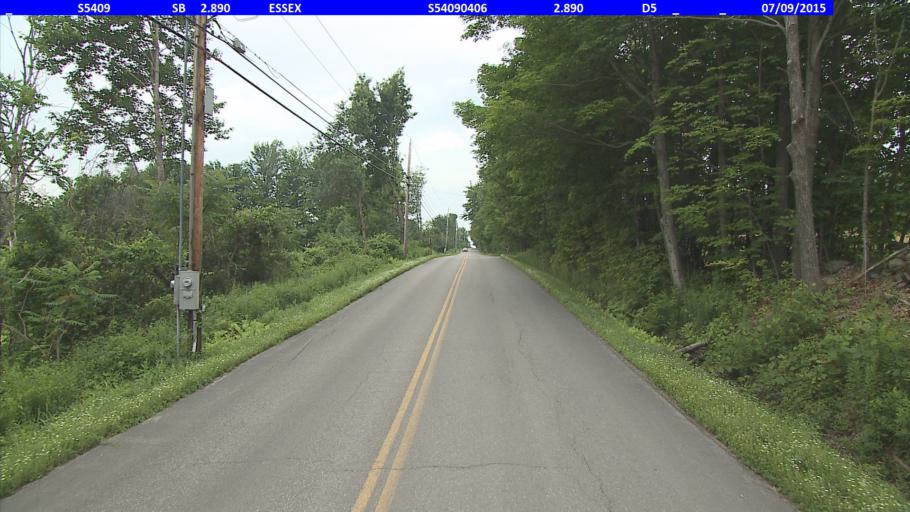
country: US
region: Vermont
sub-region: Chittenden County
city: Essex Junction
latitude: 44.5501
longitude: -73.0701
